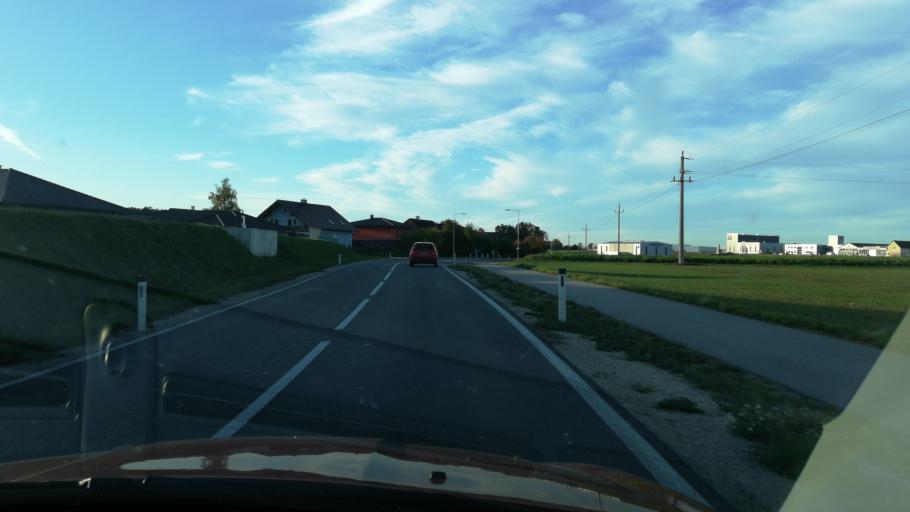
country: AT
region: Upper Austria
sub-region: Politischer Bezirk Steyr-Land
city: Bad Hall
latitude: 48.0220
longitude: 14.2324
